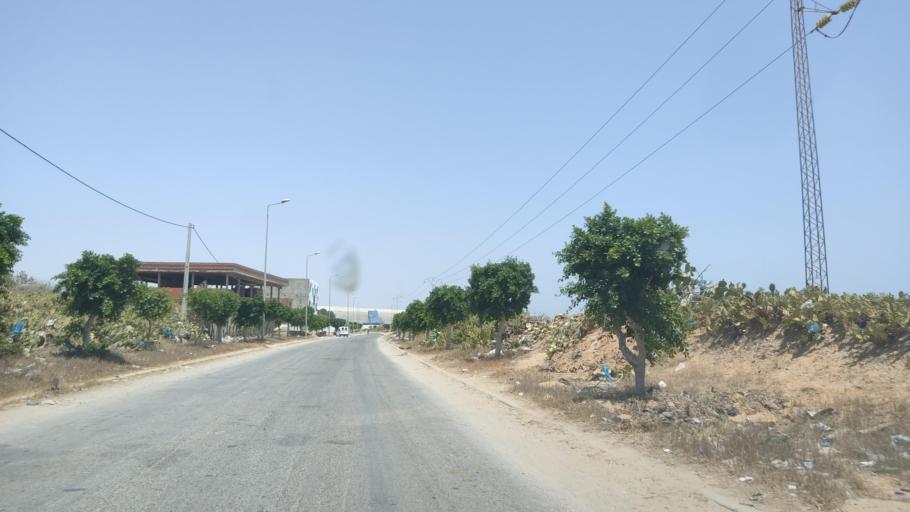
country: TN
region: Safaqis
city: Sfax
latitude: 34.6832
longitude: 10.7219
